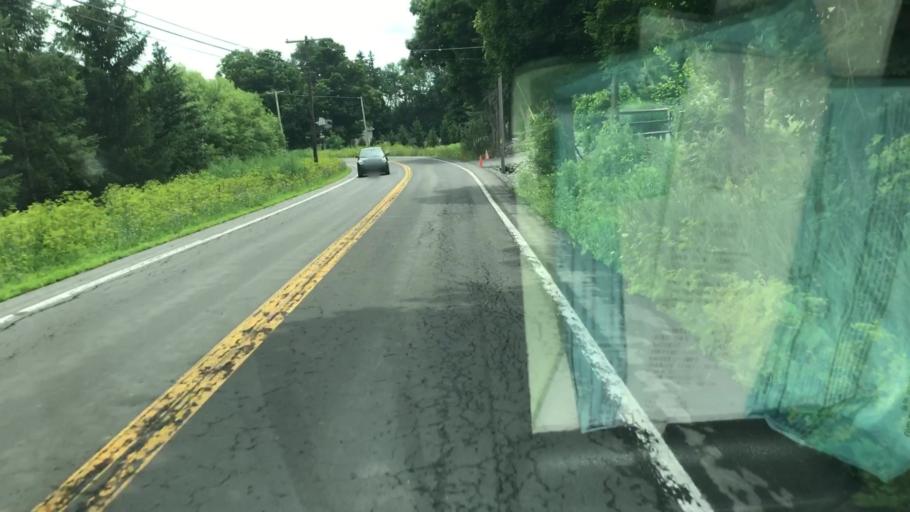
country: US
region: New York
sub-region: Onondaga County
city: Manlius
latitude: 42.9551
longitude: -75.9864
